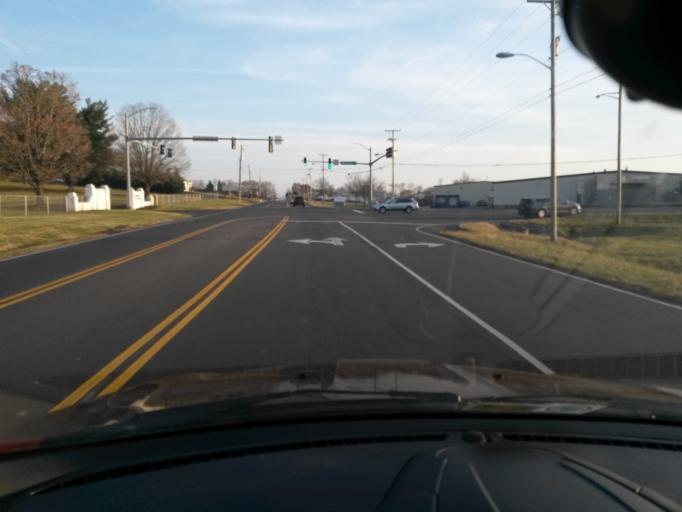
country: US
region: Virginia
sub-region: Roanoke County
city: Hollins
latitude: 37.3248
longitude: -79.9640
